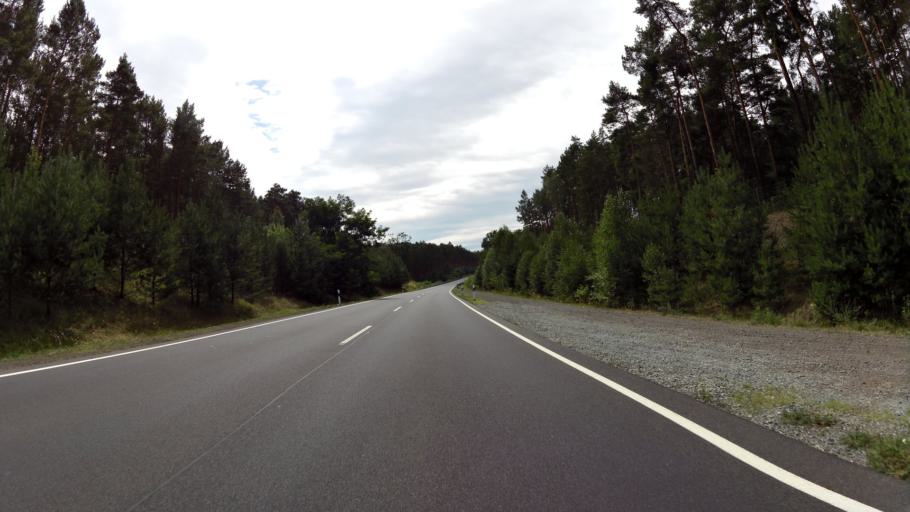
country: DE
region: Brandenburg
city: Schenkendobern
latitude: 51.9831
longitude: 14.6550
